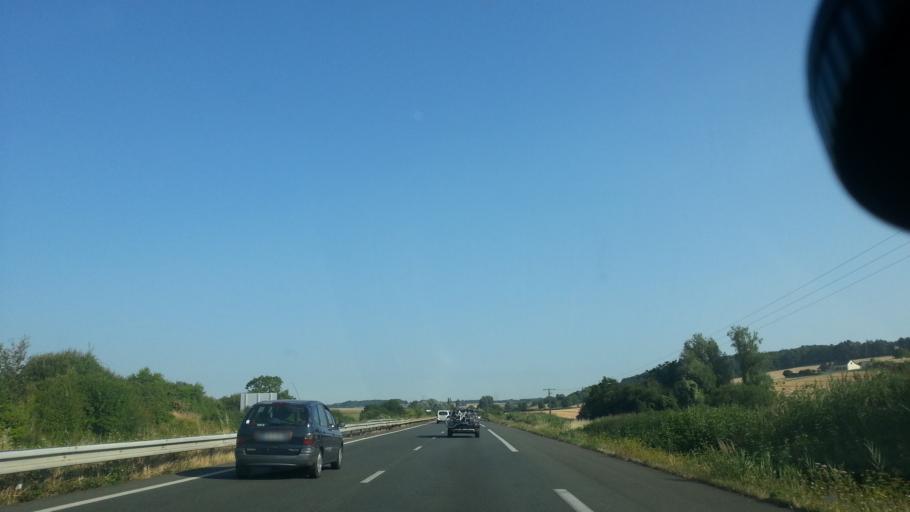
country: FR
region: Poitou-Charentes
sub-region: Departement de la Vienne
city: Antran
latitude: 46.8690
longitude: 0.5228
